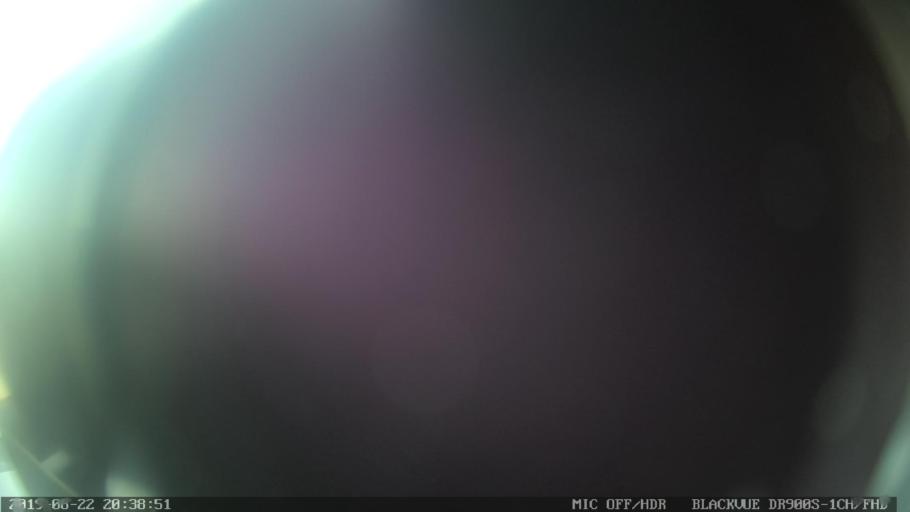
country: PT
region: Castelo Branco
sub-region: Proenca-A-Nova
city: Proenca-a-Nova
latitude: 39.6877
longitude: -7.7568
